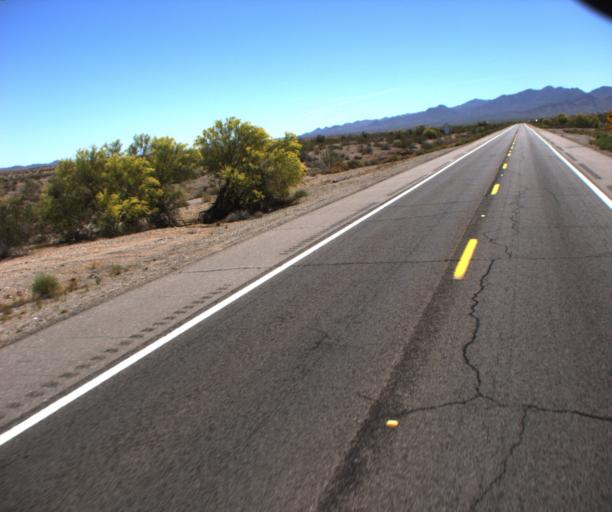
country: US
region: Arizona
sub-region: Mohave County
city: Desert Hills
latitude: 34.7175
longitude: -114.3103
